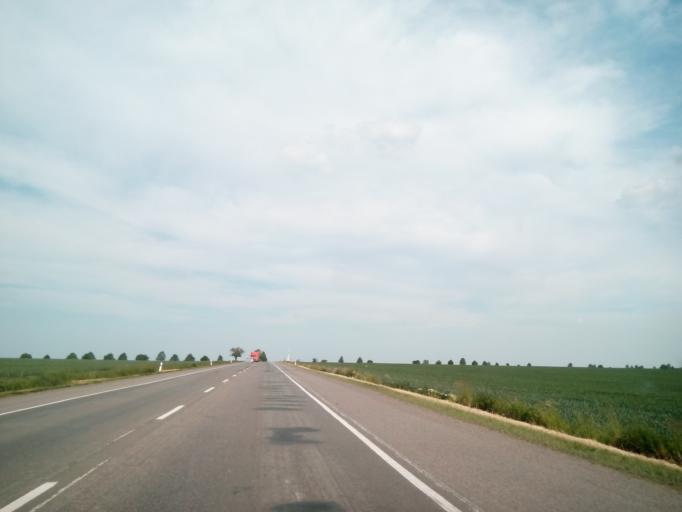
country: CZ
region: South Moravian
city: Tvarozna
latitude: 49.1850
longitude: 16.7739
